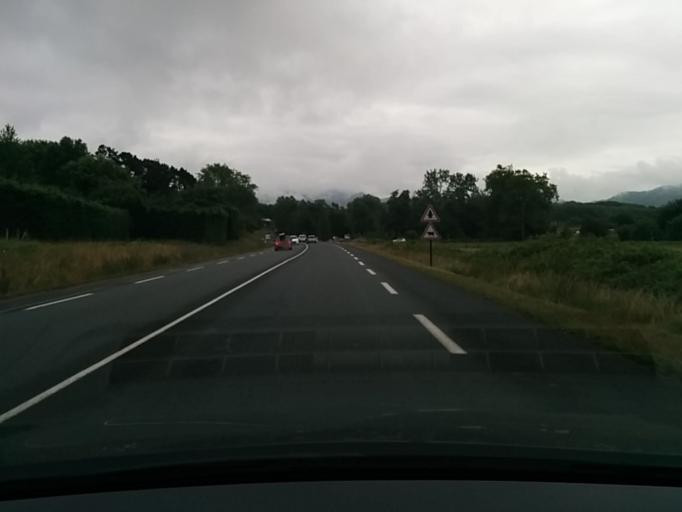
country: FR
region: Aquitaine
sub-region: Departement des Pyrenees-Atlantiques
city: Ciboure
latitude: 43.3764
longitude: -1.6864
